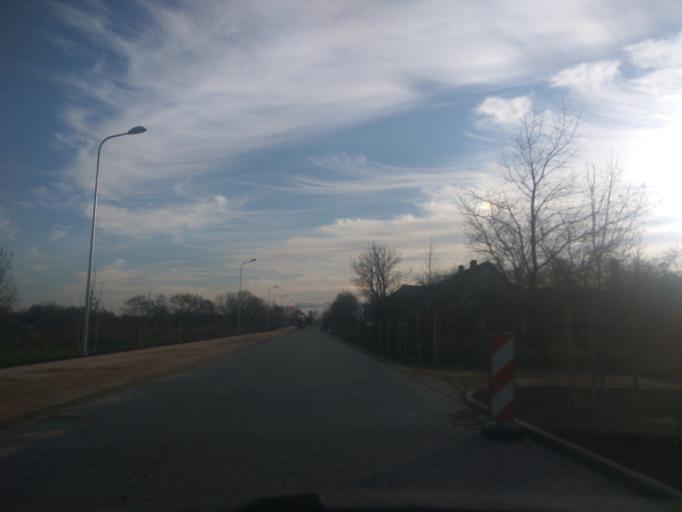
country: LV
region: Kuldigas Rajons
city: Kuldiga
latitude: 56.9837
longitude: 21.9493
